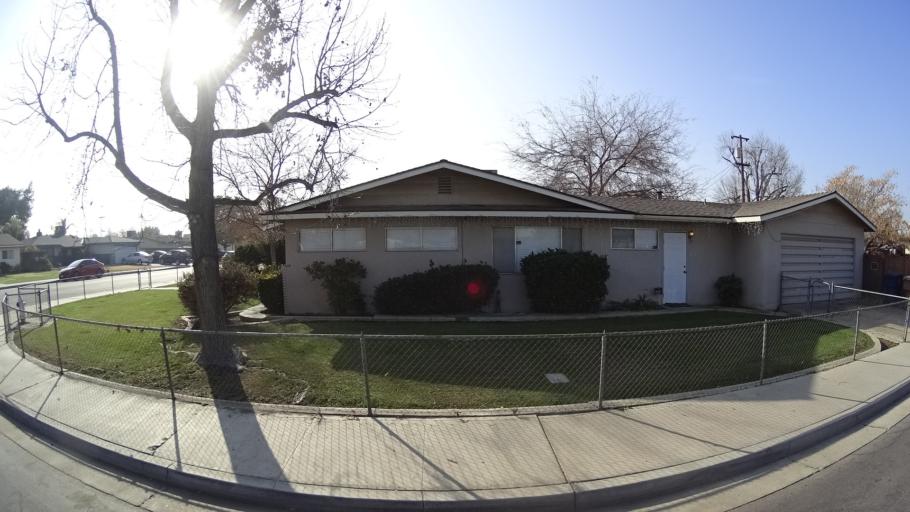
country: US
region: California
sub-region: Kern County
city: Bakersfield
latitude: 35.3264
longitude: -119.0335
